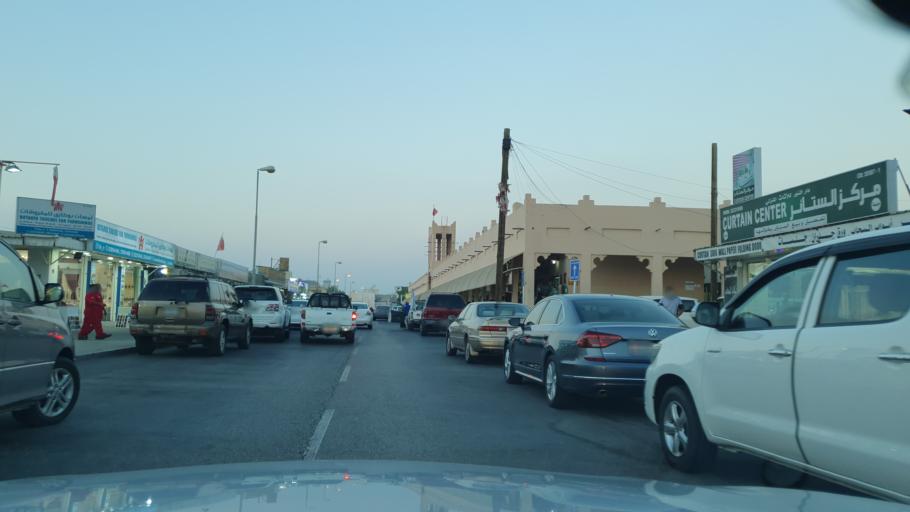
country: BH
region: Northern
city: Madinat `Isa
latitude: 26.1693
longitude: 50.5539
